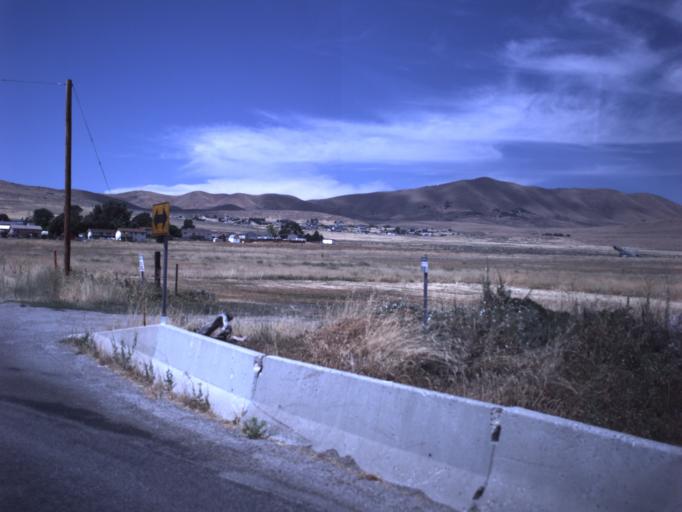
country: US
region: Utah
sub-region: Box Elder County
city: Tremonton
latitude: 41.6943
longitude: -112.2944
